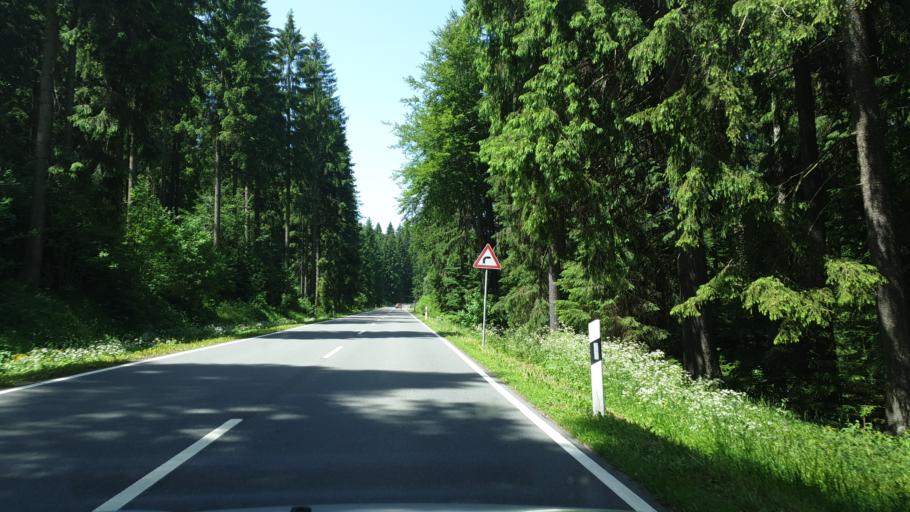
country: DE
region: Saxony
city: Zwota
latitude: 50.3905
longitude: 12.4269
